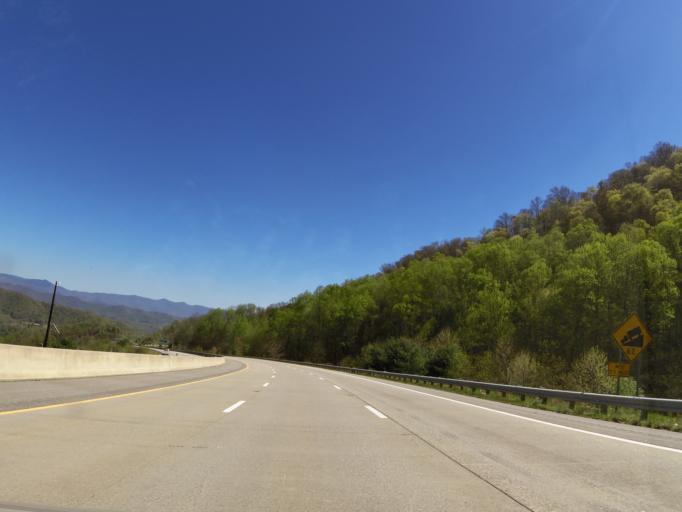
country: US
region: North Carolina
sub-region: Madison County
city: Mars Hill
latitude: 35.8804
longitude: -82.5499
